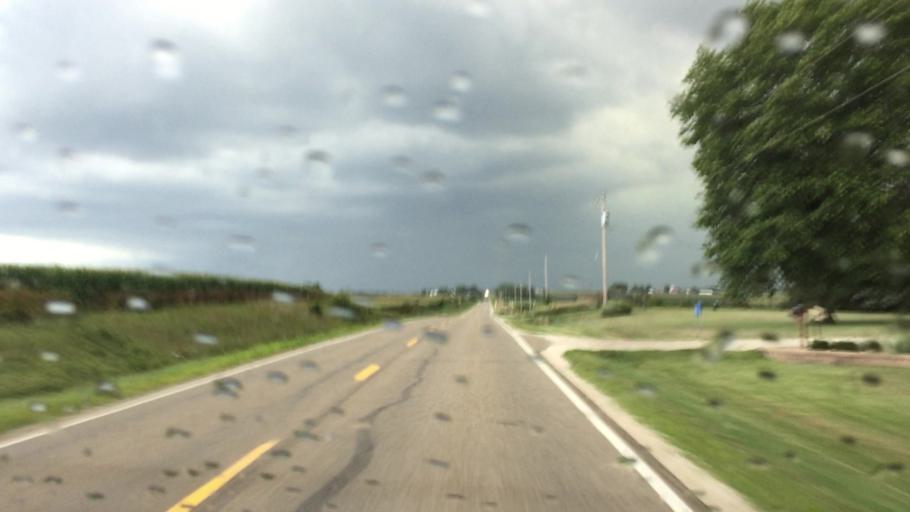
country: US
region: Iowa
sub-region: Henry County
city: Mount Pleasant
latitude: 40.7843
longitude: -91.5252
